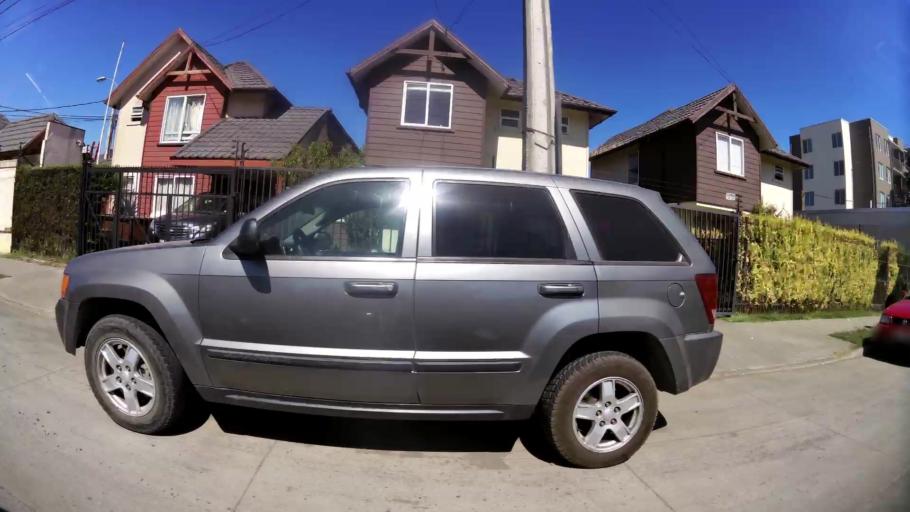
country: CL
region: Biobio
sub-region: Provincia de Concepcion
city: Concepcion
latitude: -36.7894
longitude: -73.0341
